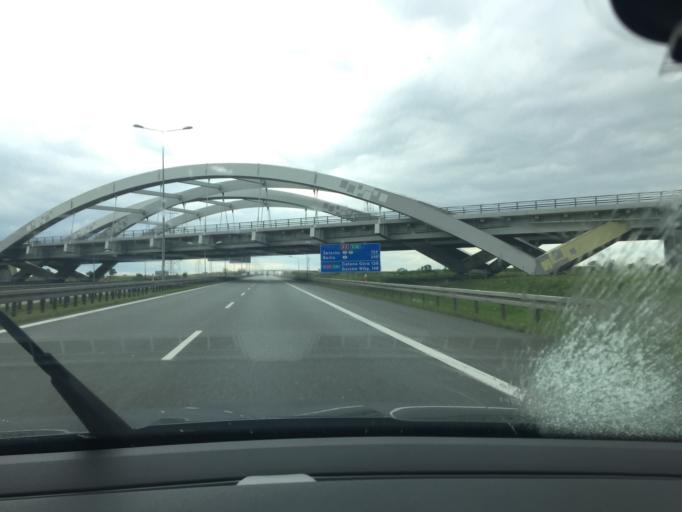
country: PL
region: Greater Poland Voivodeship
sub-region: Powiat poznanski
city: Komorniki
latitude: 52.3506
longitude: 16.7624
